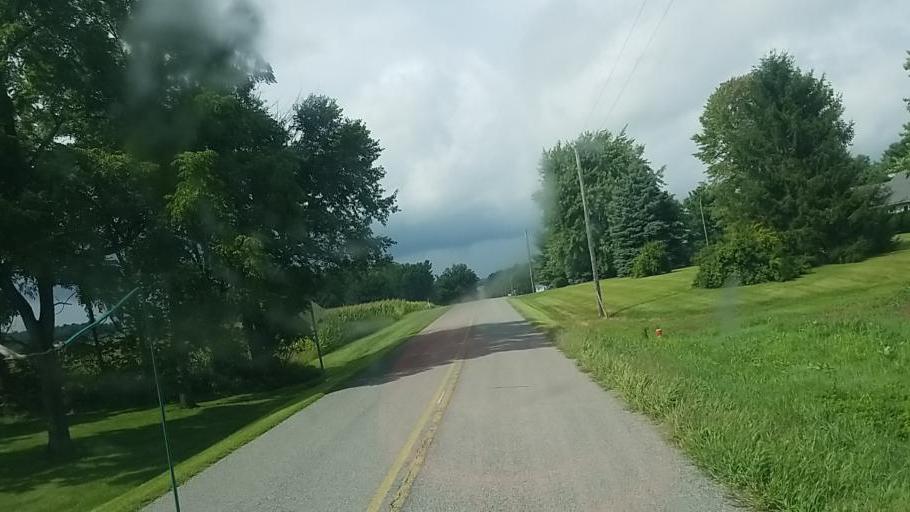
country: US
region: Ohio
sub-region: Champaign County
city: North Lewisburg
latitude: 40.2418
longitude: -83.6472
